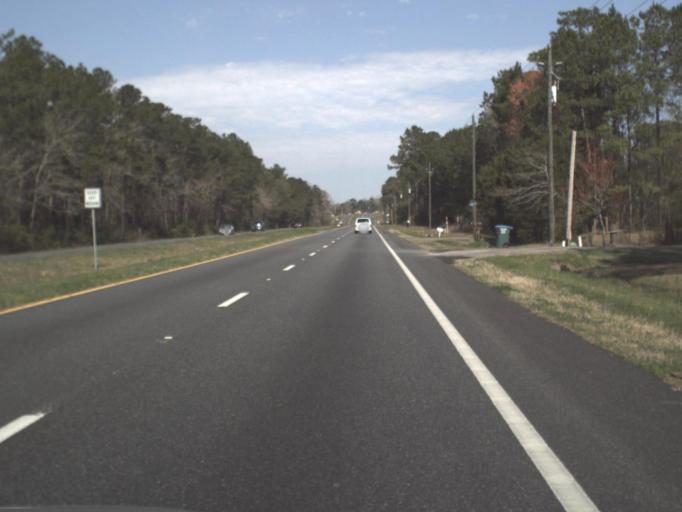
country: US
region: Florida
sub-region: Gadsden County
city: Havana
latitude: 30.5788
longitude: -84.3985
